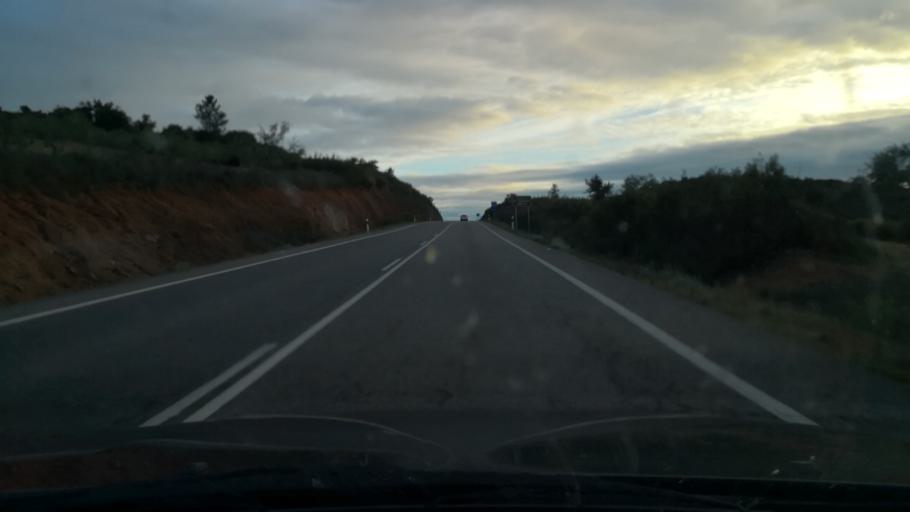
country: ES
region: Extremadura
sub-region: Provincia de Badajoz
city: Puebla de Obando
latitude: 39.1678
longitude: -6.6313
